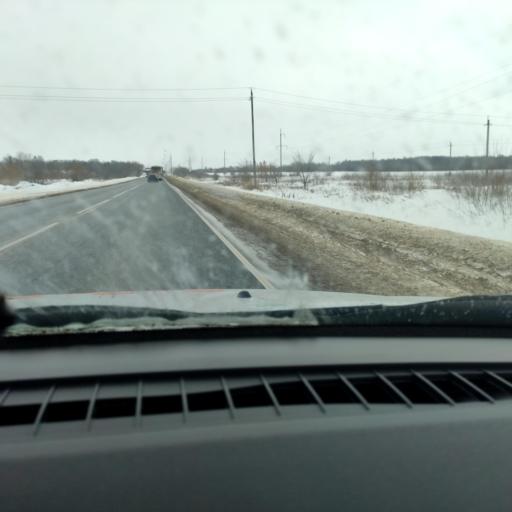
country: RU
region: Samara
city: Dubovyy Umet
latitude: 52.9795
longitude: 50.2705
